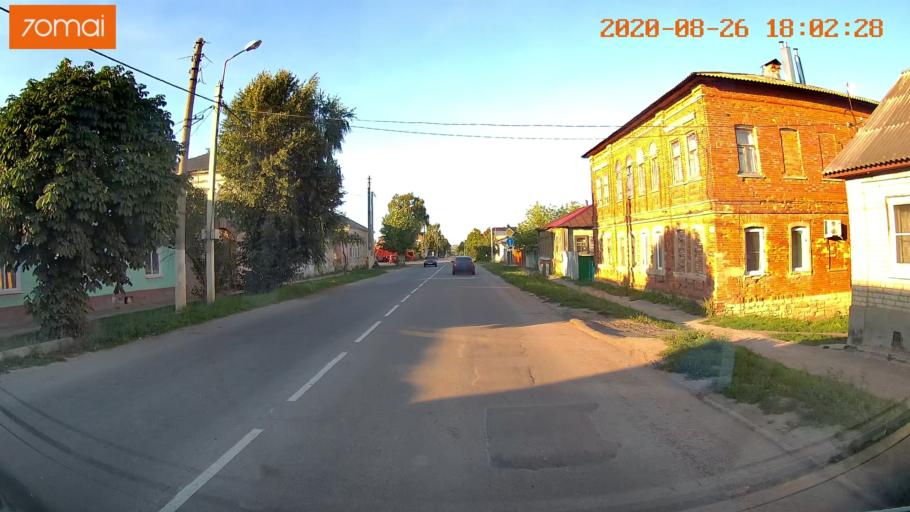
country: RU
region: Tula
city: Yefremov
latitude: 53.1391
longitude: 38.1208
